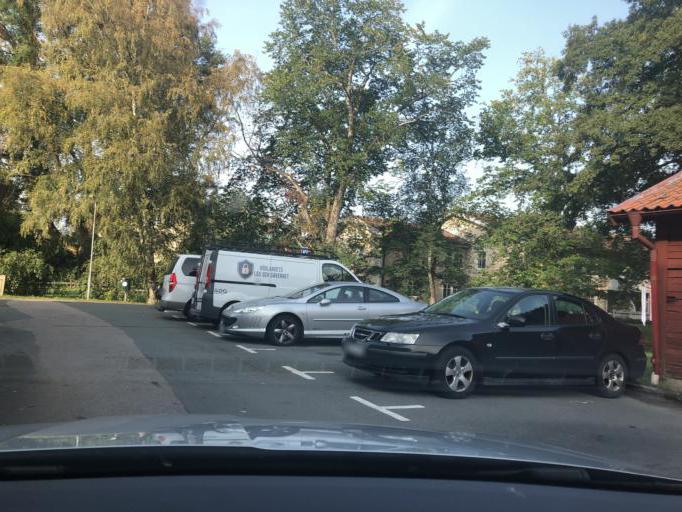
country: SE
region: Joenkoeping
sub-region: Eksjo Kommun
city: Eksjoe
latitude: 57.6685
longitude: 14.9681
